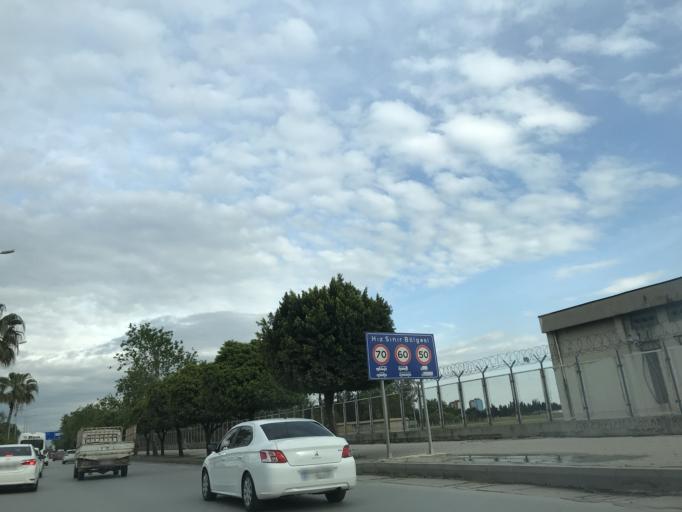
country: TR
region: Adana
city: Seyhan
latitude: 36.9940
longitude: 35.2904
